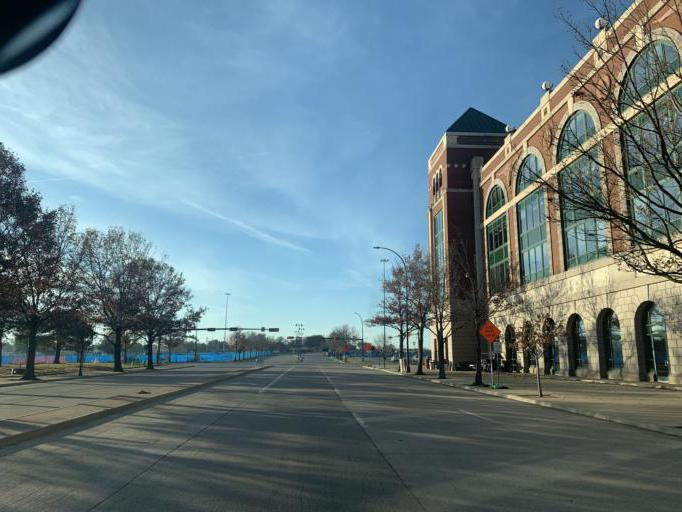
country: US
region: Texas
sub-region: Tarrant County
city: Arlington
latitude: 32.7510
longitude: -97.0811
